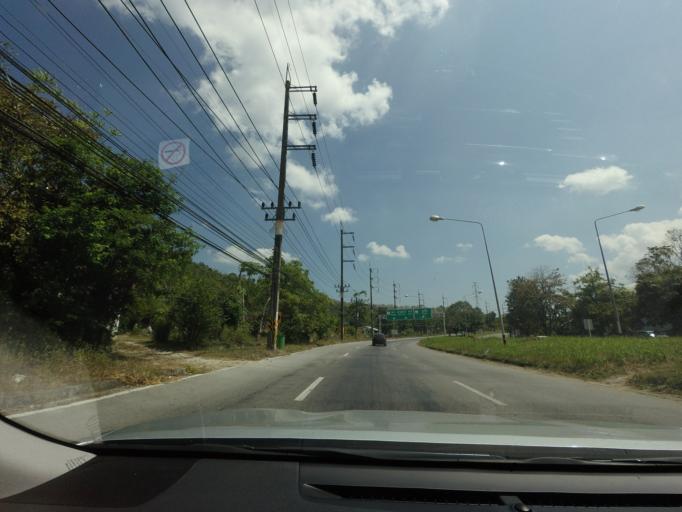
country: TH
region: Phangnga
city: Thai Mueang
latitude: 8.2717
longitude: 98.3343
